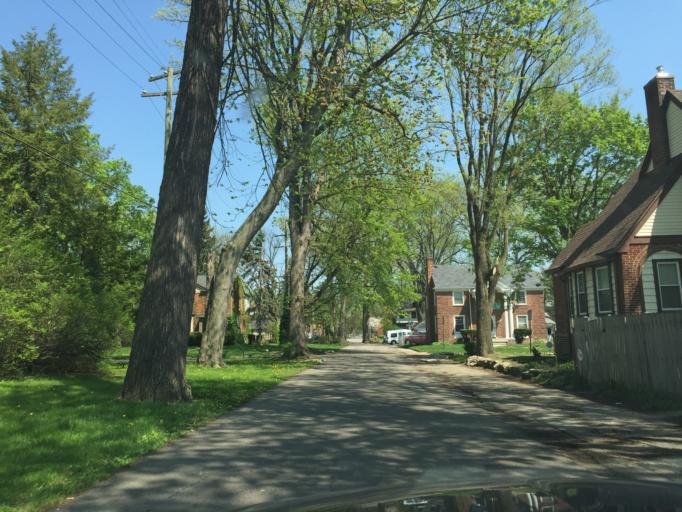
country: US
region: Michigan
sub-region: Oakland County
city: Southfield
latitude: 42.4116
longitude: -83.2309
